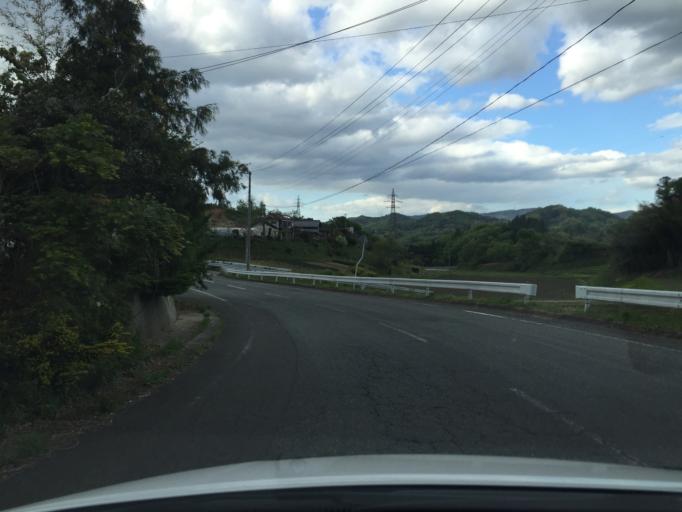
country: JP
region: Fukushima
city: Fukushima-shi
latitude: 37.6619
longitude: 140.4960
